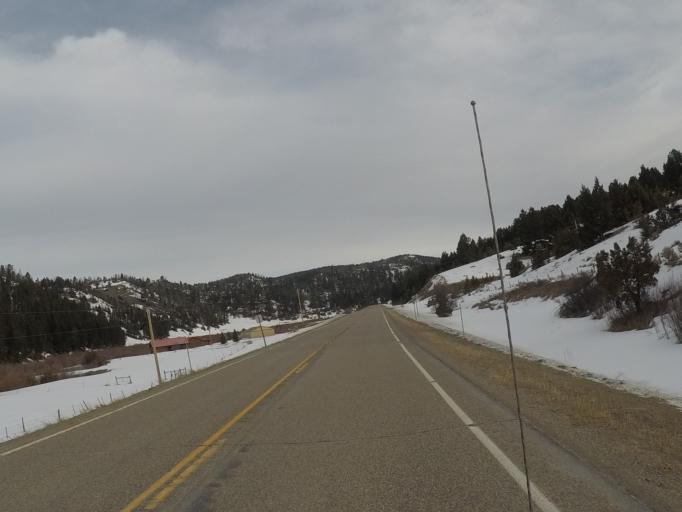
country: US
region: Montana
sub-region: Meagher County
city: White Sulphur Springs
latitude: 46.6706
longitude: -110.8777
